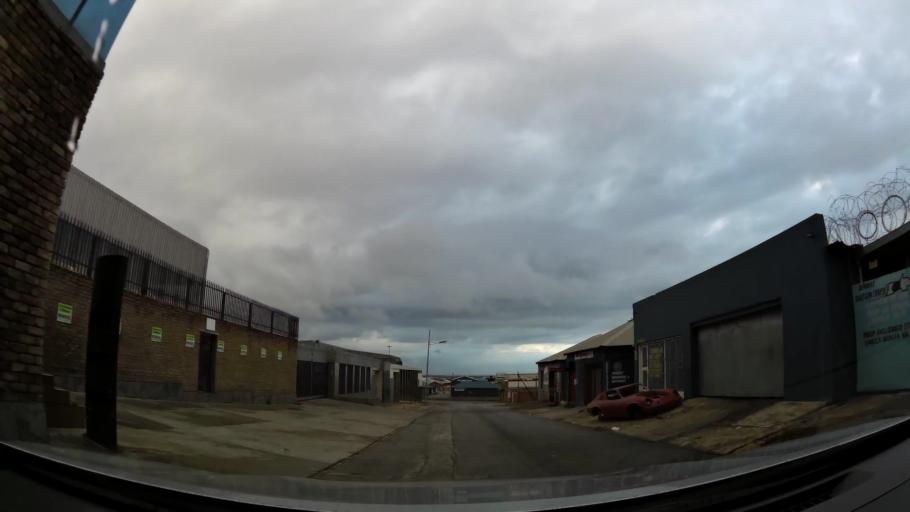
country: ZA
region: Eastern Cape
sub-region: Nelson Mandela Bay Metropolitan Municipality
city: Port Elizabeth
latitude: -33.9235
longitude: 25.5933
